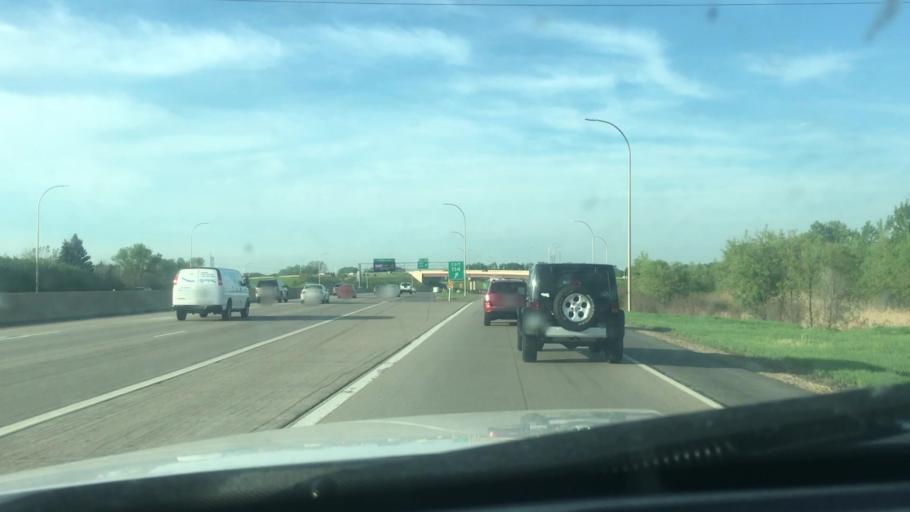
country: US
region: Minnesota
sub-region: Ramsey County
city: Vadnais Heights
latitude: 45.0431
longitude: -93.0615
